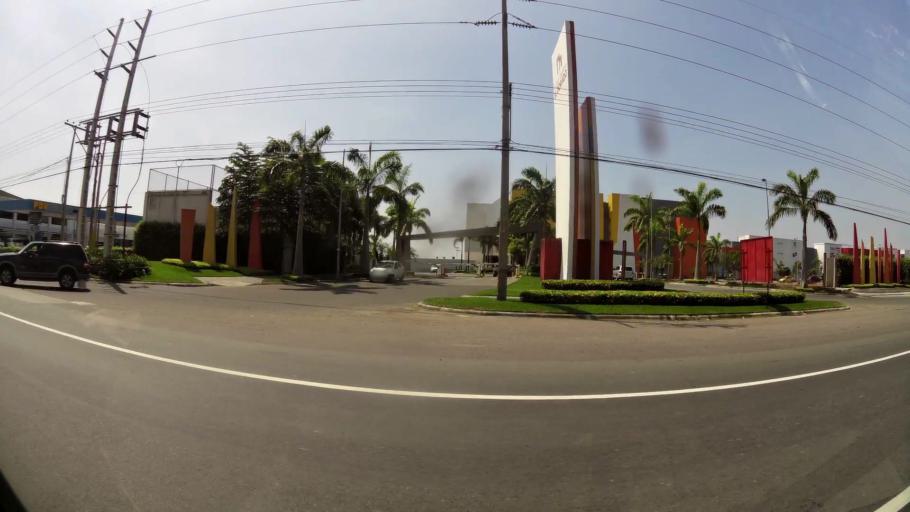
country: EC
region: Guayas
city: Eloy Alfaro
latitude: -2.0553
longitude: -79.8764
